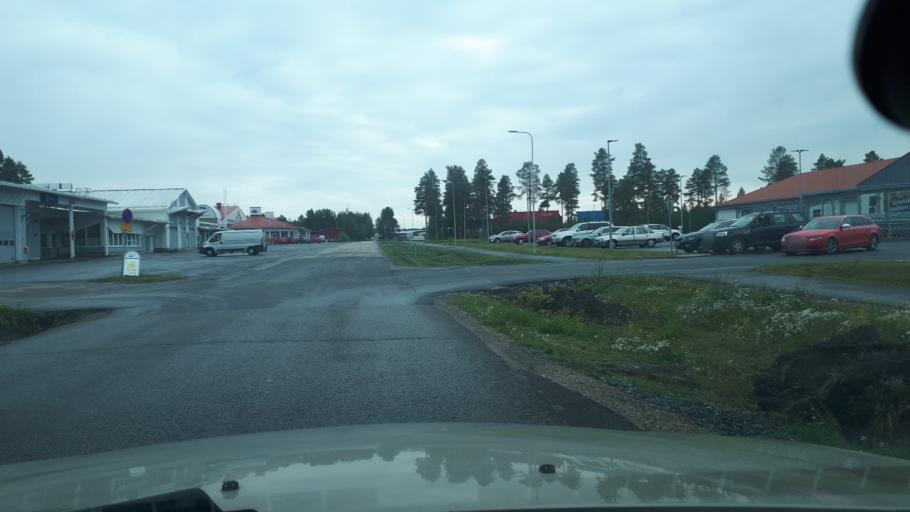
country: FI
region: Northern Ostrobothnia
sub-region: Oulu
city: Haukipudas
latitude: 65.1664
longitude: 25.3453
